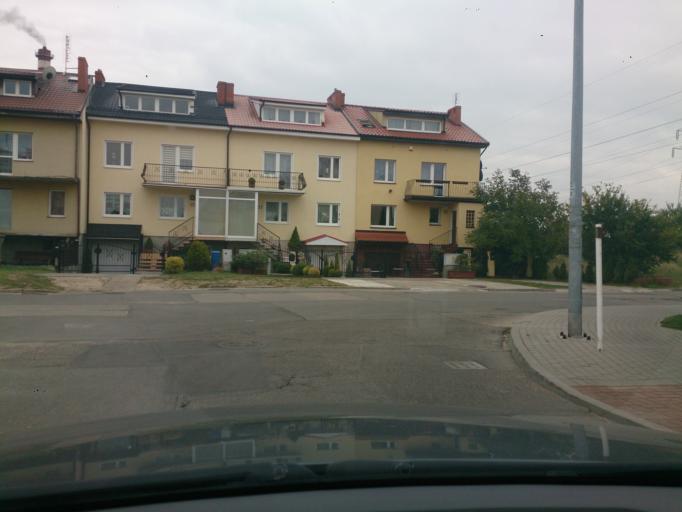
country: PL
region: Pomeranian Voivodeship
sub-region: Powiat wejherowski
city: Reda
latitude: 54.6007
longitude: 18.3609
